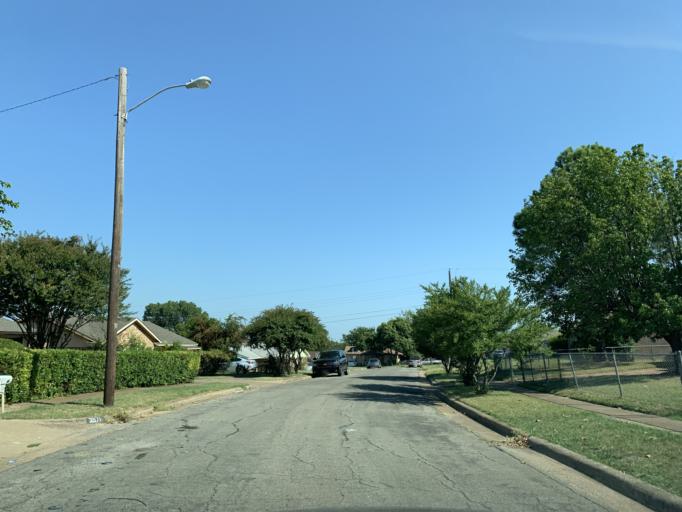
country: US
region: Texas
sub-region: Dallas County
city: Hutchins
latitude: 32.6658
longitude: -96.7477
